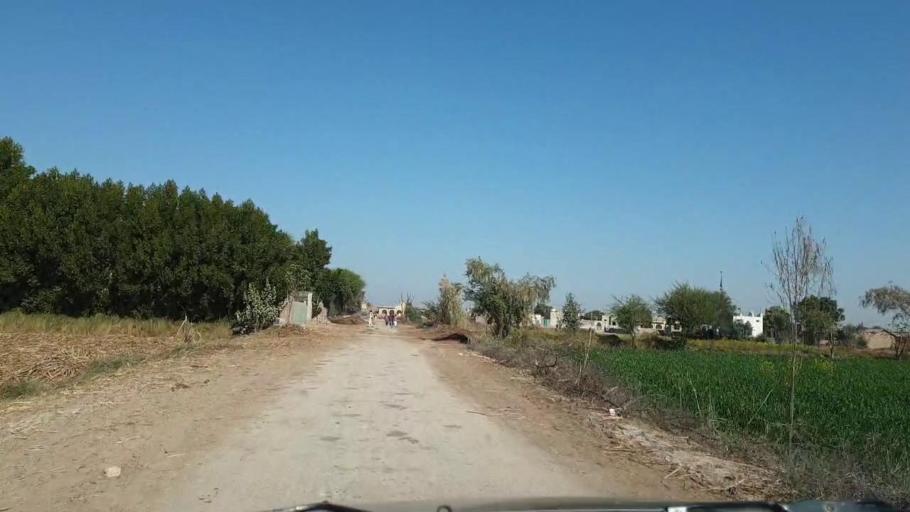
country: PK
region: Sindh
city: Sinjhoro
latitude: 26.1083
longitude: 68.8426
